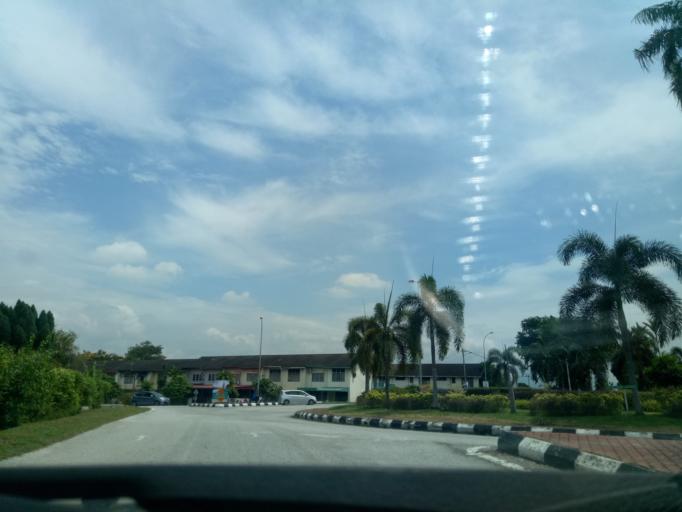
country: MY
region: Perak
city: Ipoh
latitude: 4.6025
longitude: 101.1119
